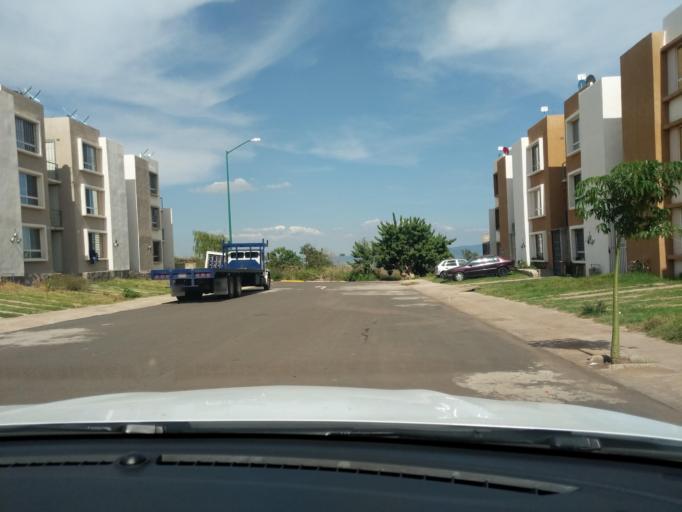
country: MX
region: Jalisco
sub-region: El Salto
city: El Muey
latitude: 20.5209
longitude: -103.2187
